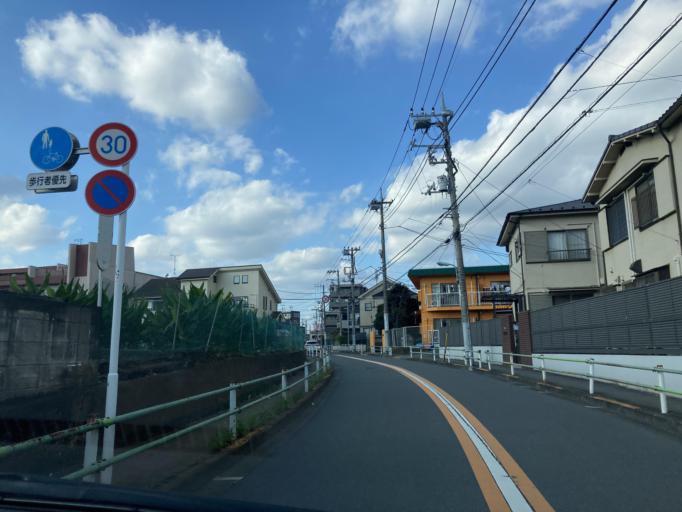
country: JP
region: Tokyo
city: Chofugaoka
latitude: 35.6448
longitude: 139.5511
